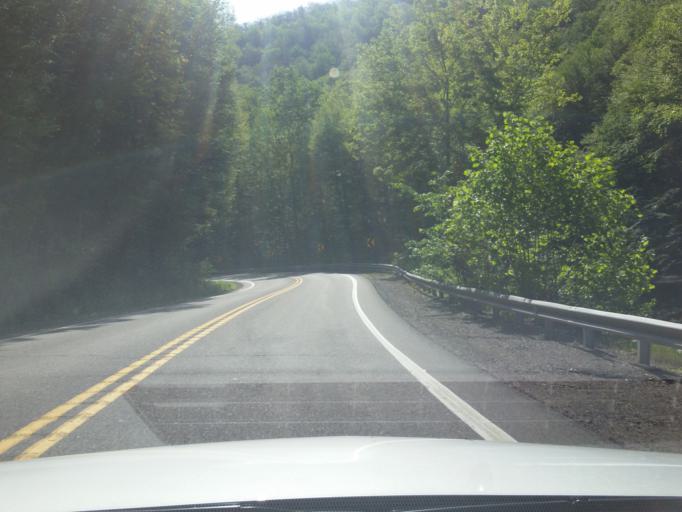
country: US
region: Pennsylvania
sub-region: Luzerne County
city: Nanticoke
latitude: 41.2328
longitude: -76.0061
